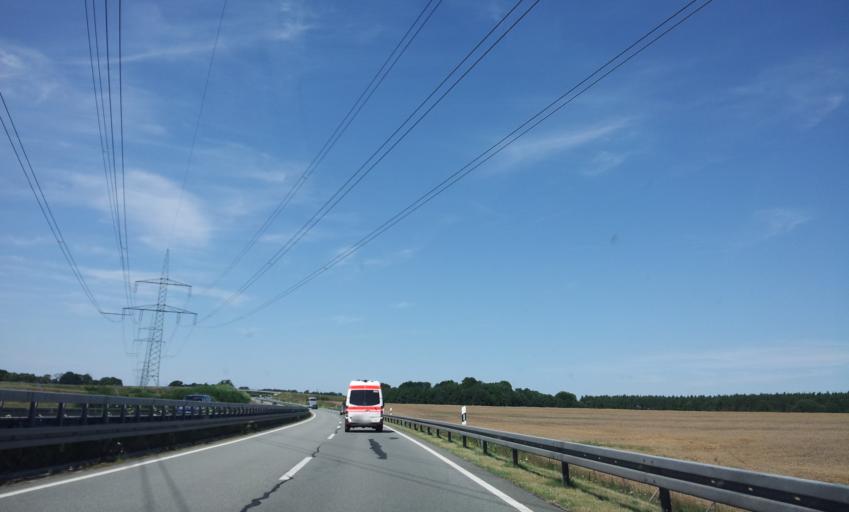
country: DE
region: Mecklenburg-Vorpommern
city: Brandshagen
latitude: 54.1999
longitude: 13.1579
